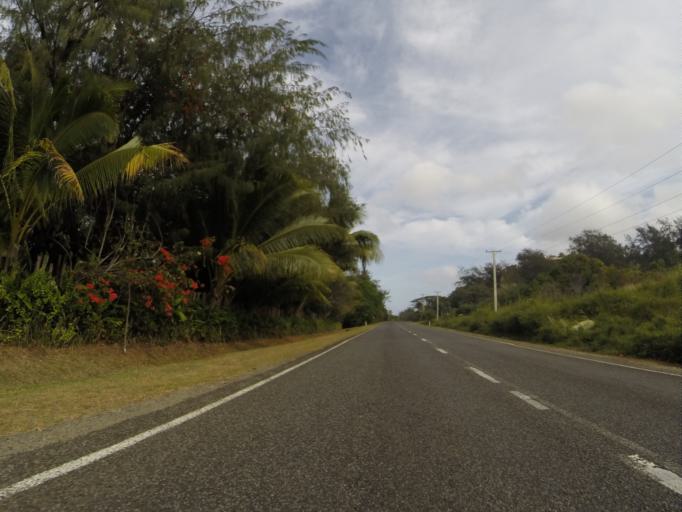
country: FJ
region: Western
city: Nadi
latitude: -18.1822
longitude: 177.5783
